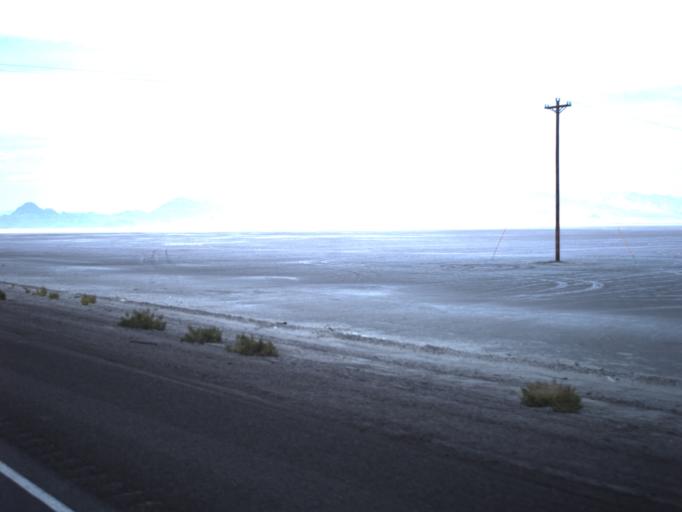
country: US
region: Utah
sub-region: Tooele County
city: Wendover
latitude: 40.7376
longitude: -113.7648
